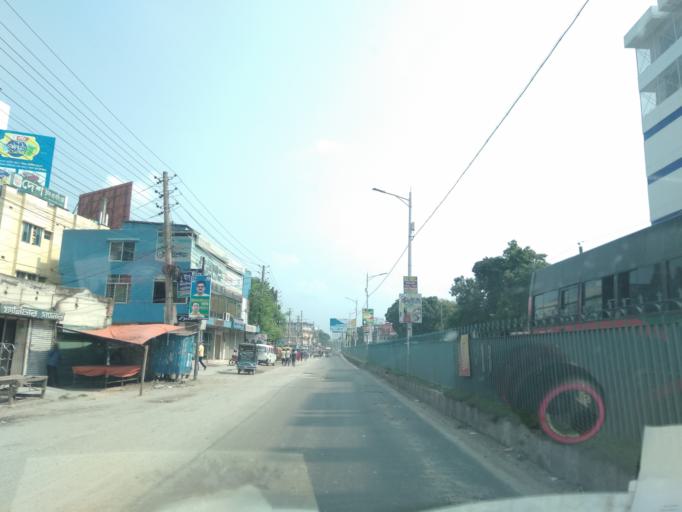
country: BD
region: Rangpur Division
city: Rangpur
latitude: 25.7627
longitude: 89.2315
